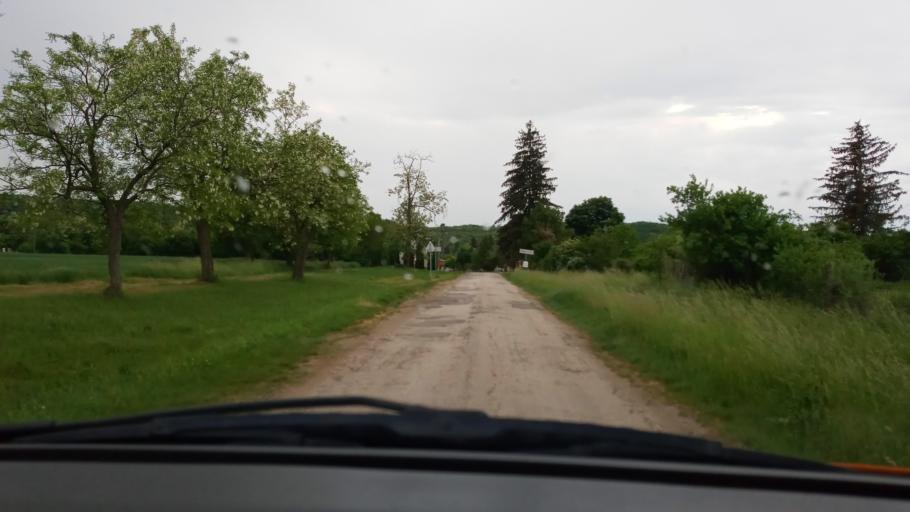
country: HU
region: Baranya
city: Harkany
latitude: 45.9013
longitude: 18.1371
